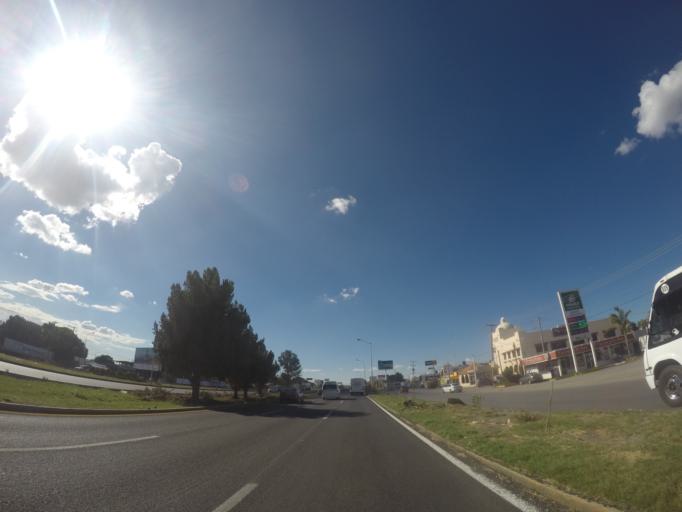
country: MX
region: San Luis Potosi
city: La Pila
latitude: 22.0868
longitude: -100.8798
